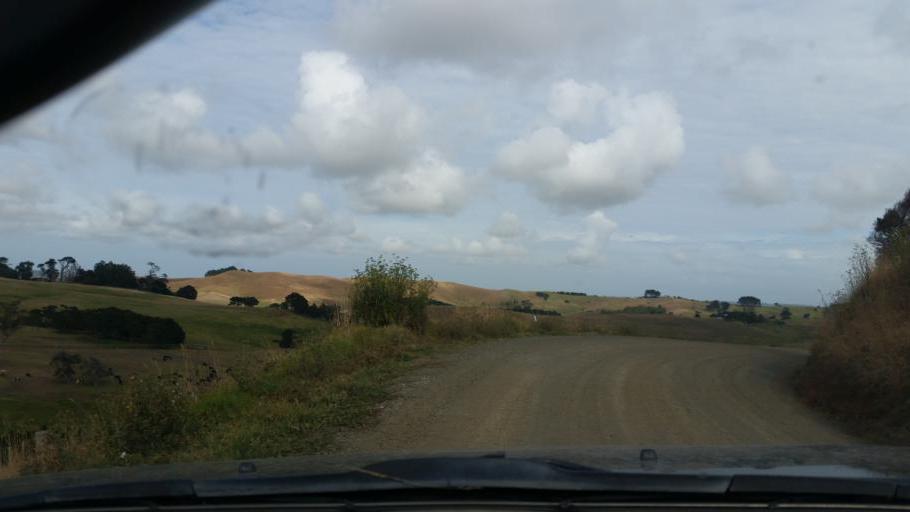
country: NZ
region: Northland
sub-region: Kaipara District
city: Dargaville
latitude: -35.9837
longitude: 173.9573
